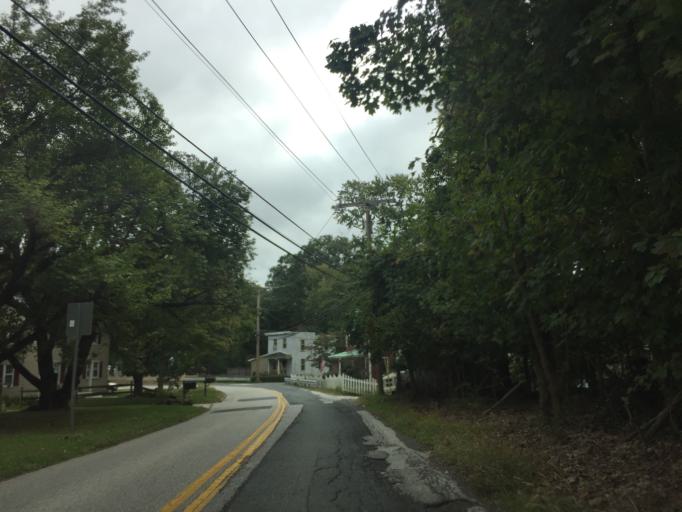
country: US
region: Maryland
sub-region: Baltimore County
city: Cockeysville
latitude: 39.4810
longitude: -76.6367
